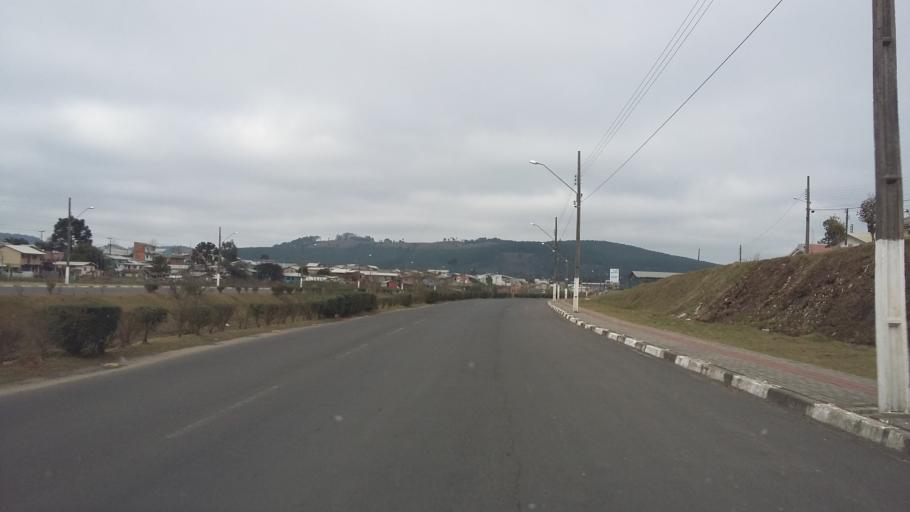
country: BR
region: Santa Catarina
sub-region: Lages
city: Lages
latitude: -27.8297
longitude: -50.3210
